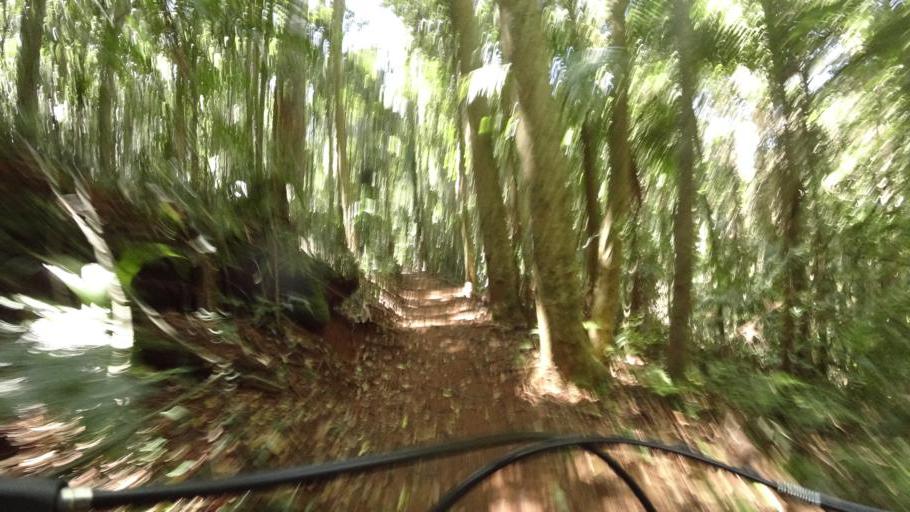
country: AU
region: Queensland
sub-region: Moreton Bay
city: Highvale
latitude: -27.4053
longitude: 152.8094
